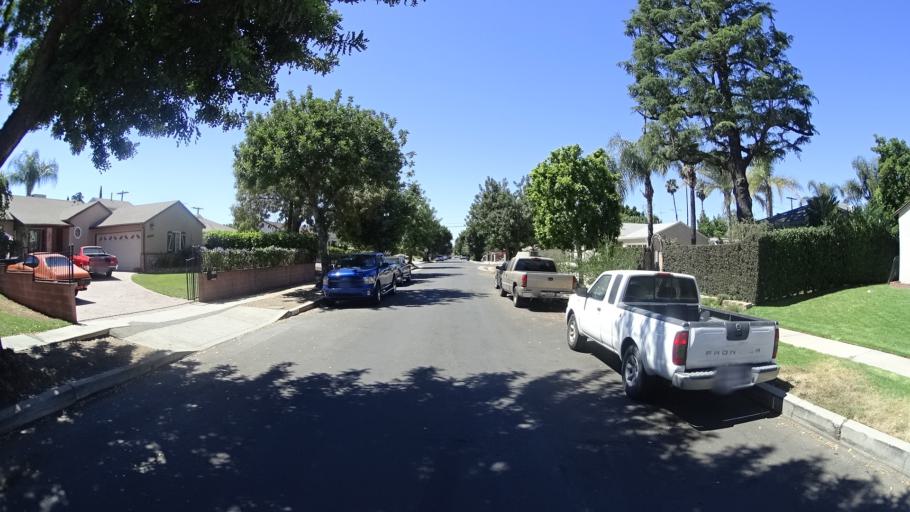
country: US
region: California
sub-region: Los Angeles County
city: San Fernando
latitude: 34.2543
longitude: -118.4565
